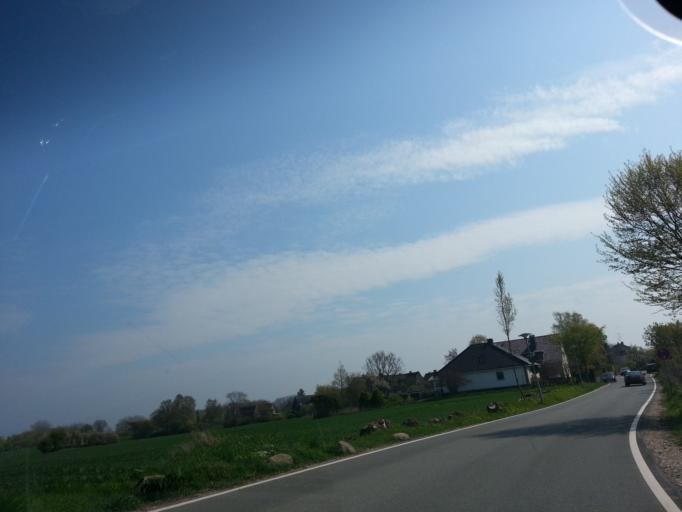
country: DE
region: Schleswig-Holstein
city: Travemuende
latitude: 53.9896
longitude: 10.8589
